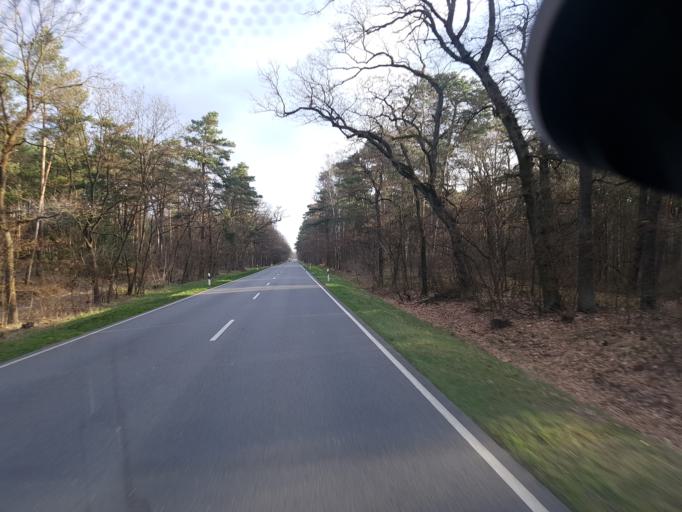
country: DE
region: Brandenburg
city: Luebben
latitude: 51.9654
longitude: 13.9466
